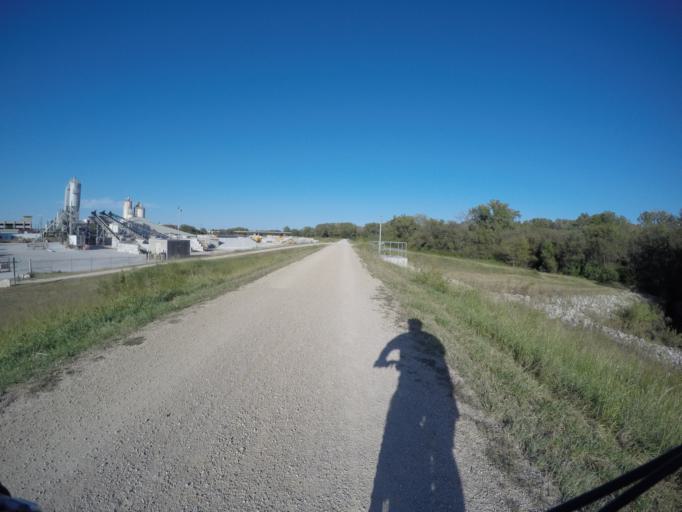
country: US
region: Kansas
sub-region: Riley County
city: Manhattan
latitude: 39.1717
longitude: -96.5606
